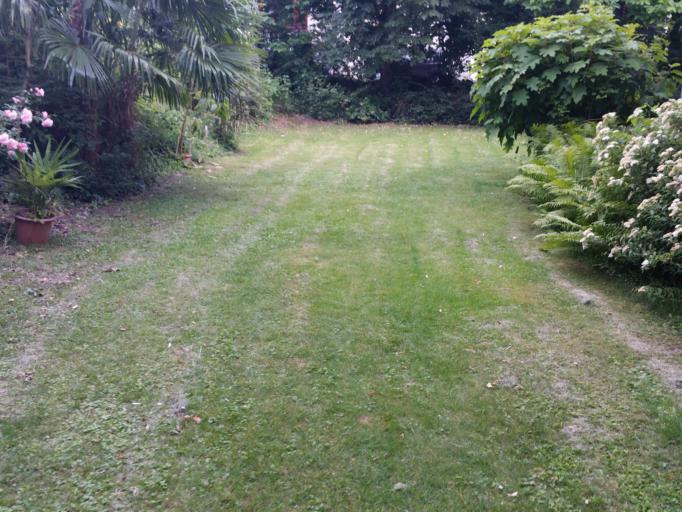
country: IT
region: Trentino-Alto Adige
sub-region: Bolzano
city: Merano
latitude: 46.6691
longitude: 11.1692
